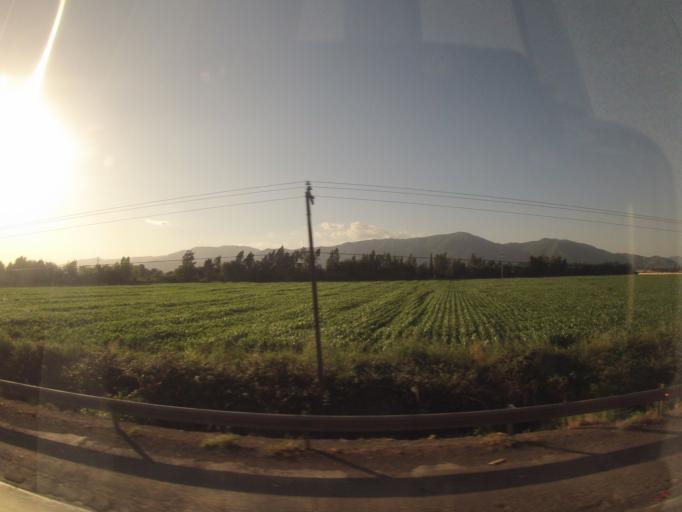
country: CL
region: O'Higgins
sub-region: Provincia de Colchagua
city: Chimbarongo
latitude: -34.5879
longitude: -70.9669
